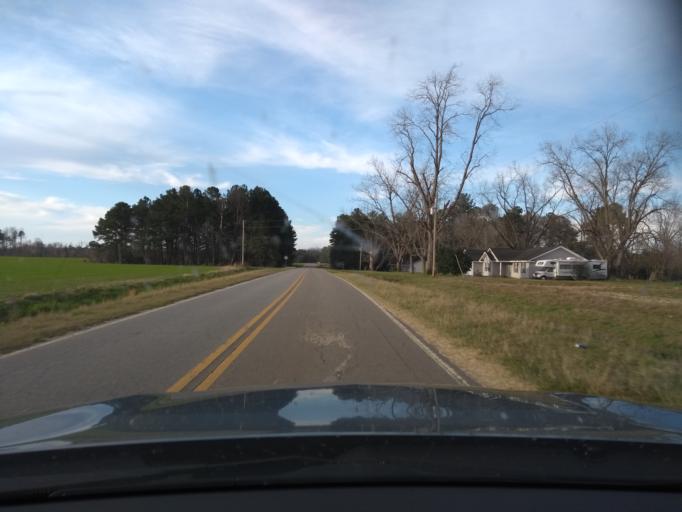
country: US
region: Georgia
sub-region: Evans County
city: Claxton
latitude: 32.2418
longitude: -81.7694
